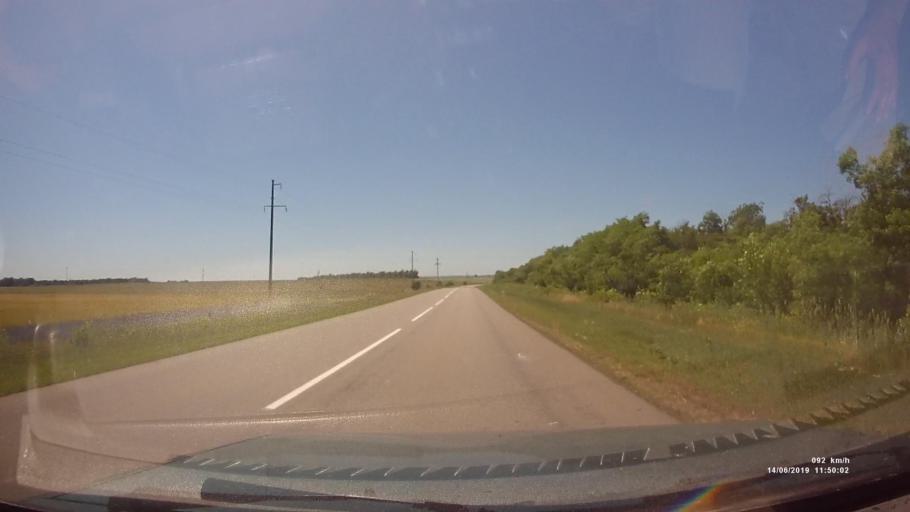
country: RU
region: Rostov
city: Kazanskaya
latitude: 49.8491
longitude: 41.2718
